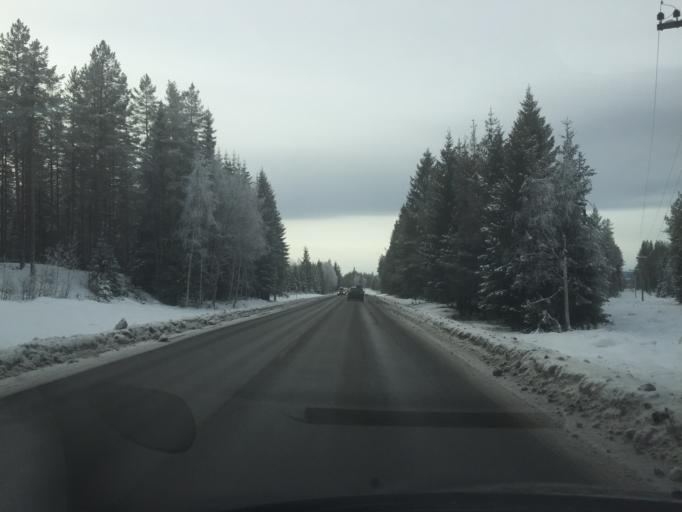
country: NO
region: Hedmark
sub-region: Elverum
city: Elverum
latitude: 60.9808
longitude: 11.7458
